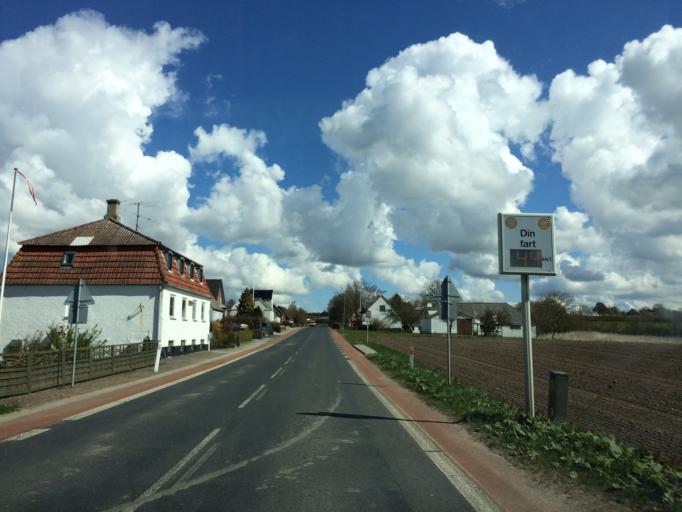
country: DK
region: South Denmark
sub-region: Assens Kommune
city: Harby
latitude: 55.1938
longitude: 10.1537
